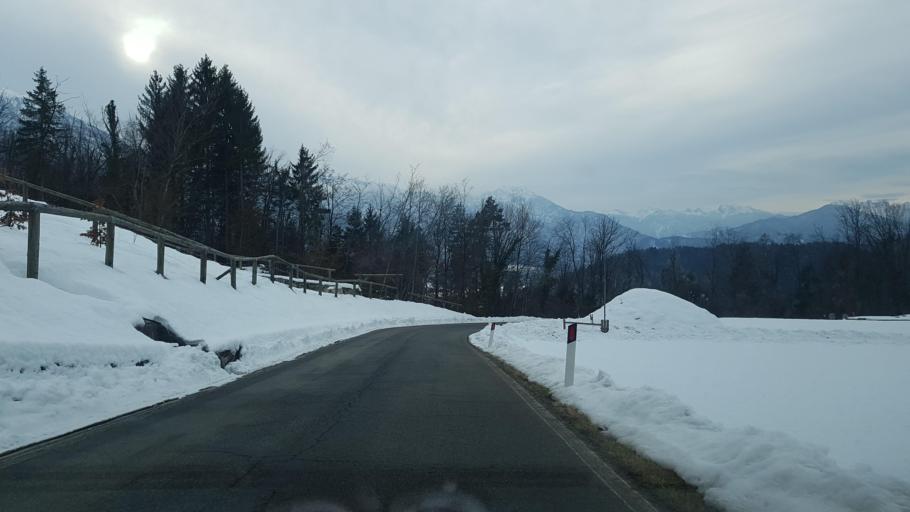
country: IT
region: Friuli Venezia Giulia
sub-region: Provincia di Udine
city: Villa Santina
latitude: 46.4217
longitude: 12.9215
